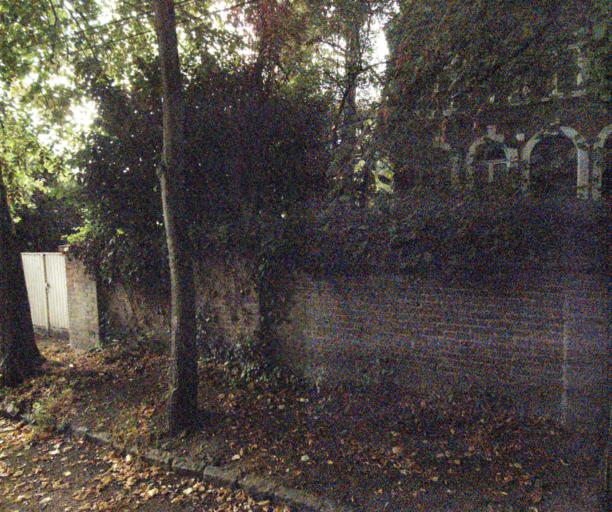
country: FR
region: Nord-Pas-de-Calais
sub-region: Departement du Nord
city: La Madeleine
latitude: 50.6480
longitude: 3.0831
